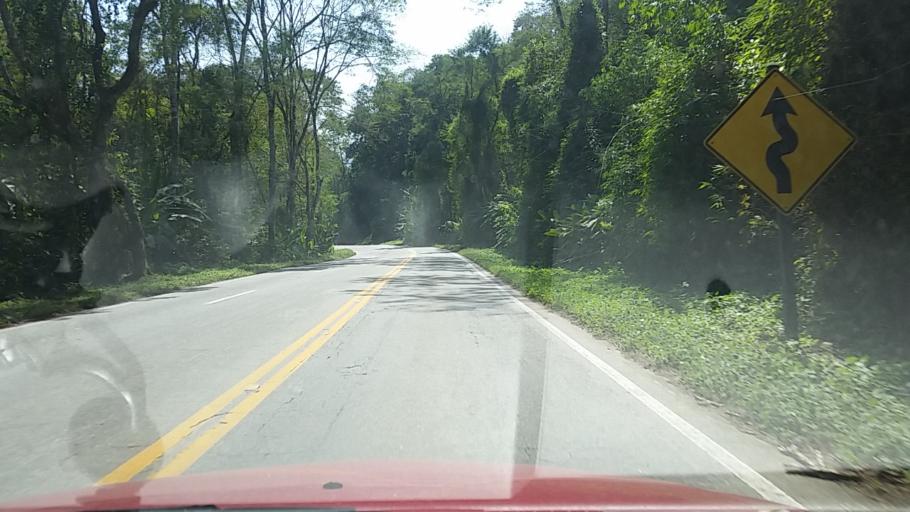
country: BR
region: Sao Paulo
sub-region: Miracatu
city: Miracatu
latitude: -24.3485
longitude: -47.4983
